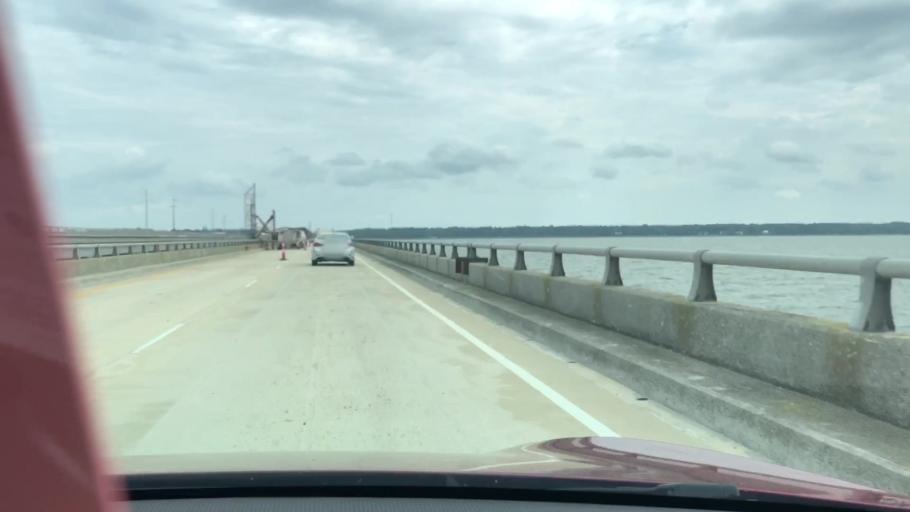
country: US
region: North Carolina
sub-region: Dare County
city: Southern Shores
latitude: 36.0867
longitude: -75.7632
